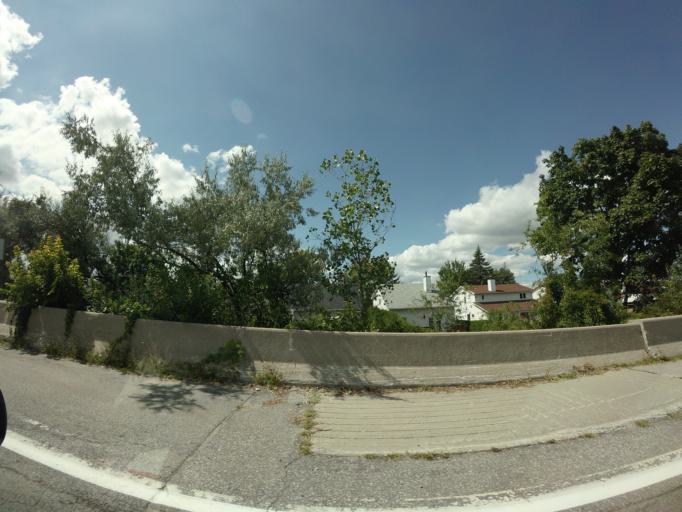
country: CA
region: Quebec
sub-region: Outaouais
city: Gatineau
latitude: 45.4705
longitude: -75.5474
